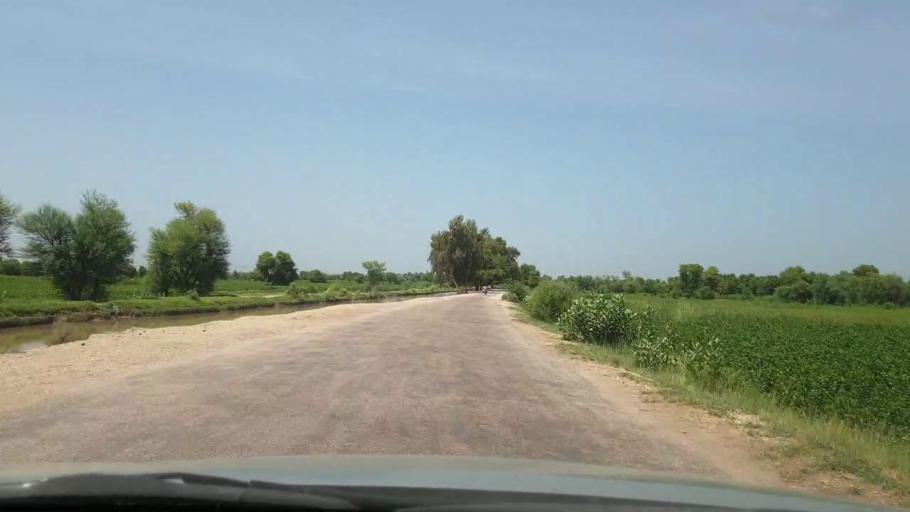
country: PK
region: Sindh
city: Pano Aqil
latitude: 27.6931
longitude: 69.1106
